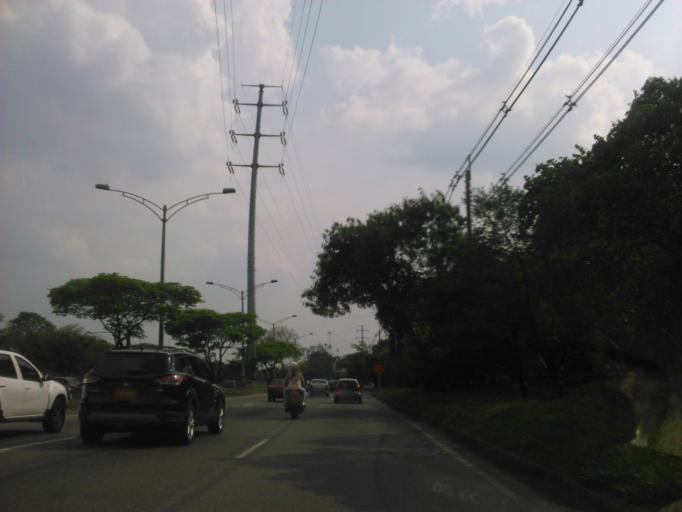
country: CO
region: Antioquia
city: Medellin
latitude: 6.2569
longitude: -75.5764
